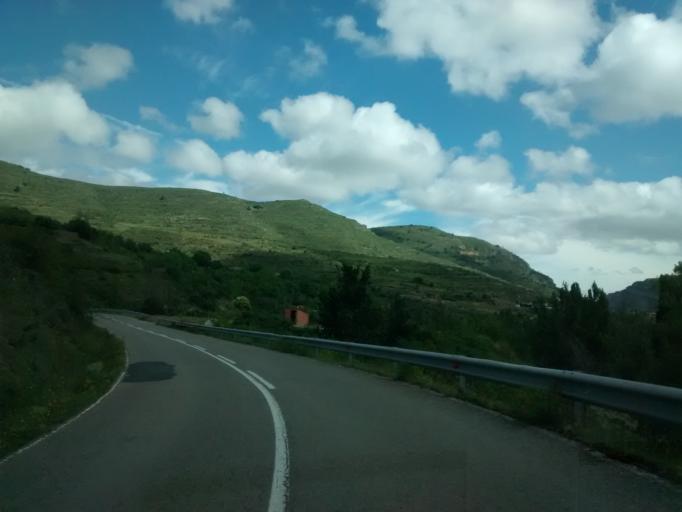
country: ES
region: La Rioja
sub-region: Provincia de La Rioja
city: Soto en Cameros
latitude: 42.2790
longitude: -2.4326
